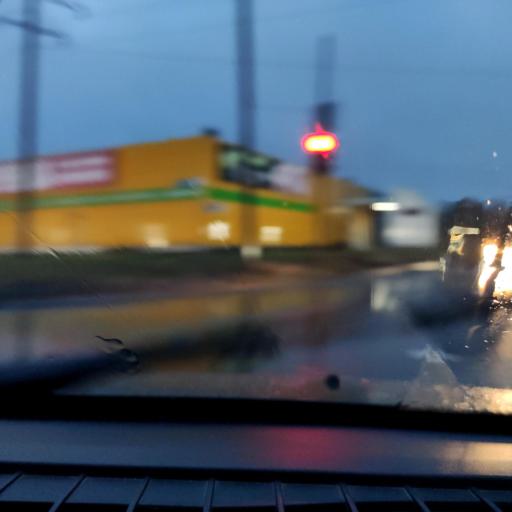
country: RU
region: Samara
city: Tol'yatti
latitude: 53.5699
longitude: 49.2915
